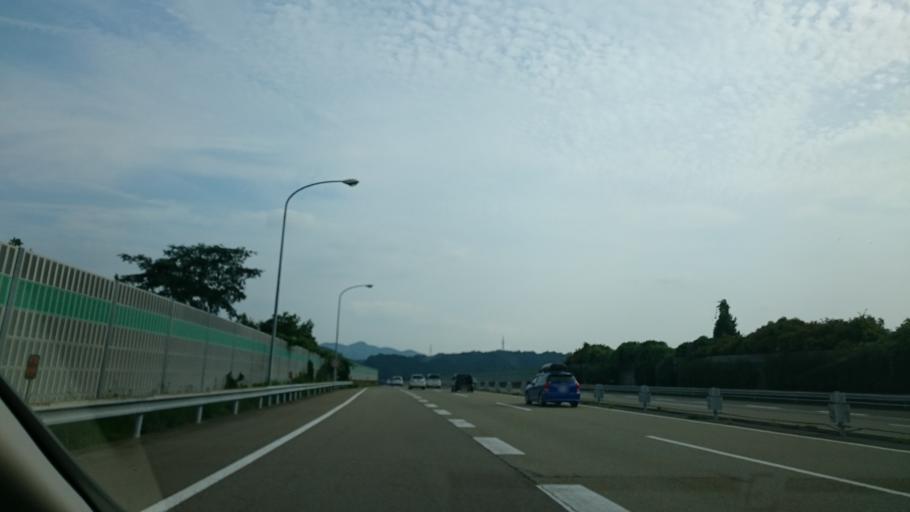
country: JP
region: Gifu
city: Mino
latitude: 35.4879
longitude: 136.8949
